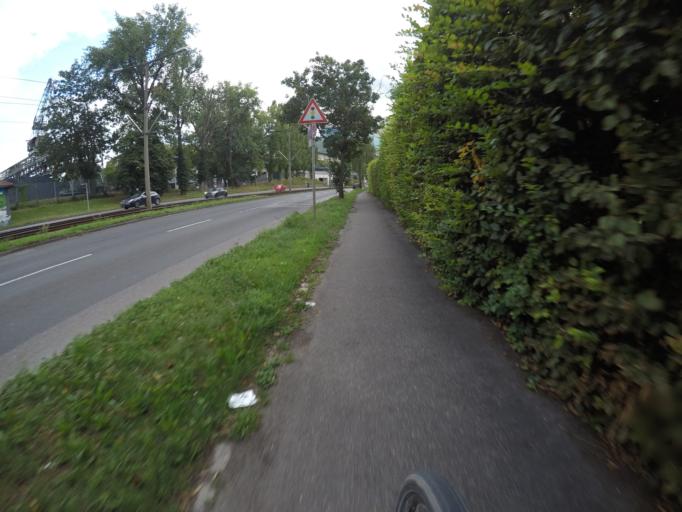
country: DE
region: Baden-Wuerttemberg
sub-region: Regierungsbezirk Stuttgart
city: Stuttgart Muehlhausen
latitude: 48.8177
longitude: 9.2238
